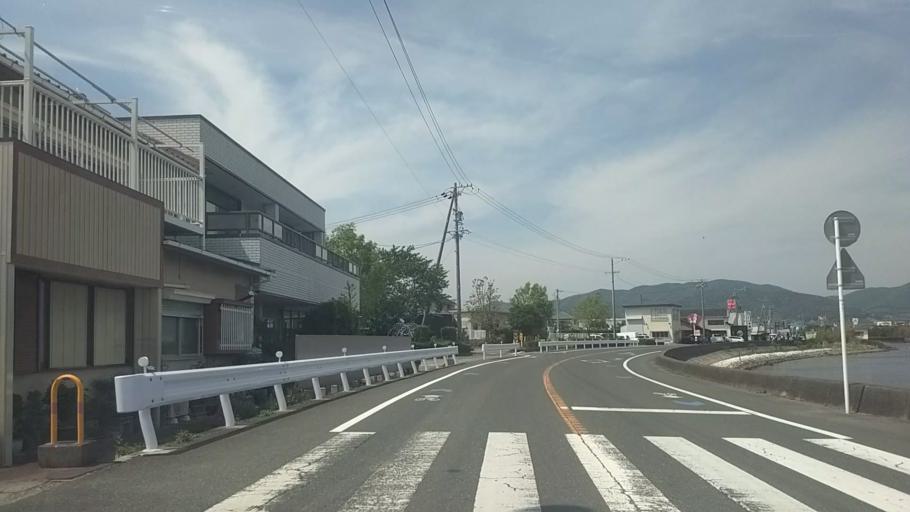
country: JP
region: Shizuoka
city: Kosai-shi
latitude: 34.7971
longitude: 137.5485
